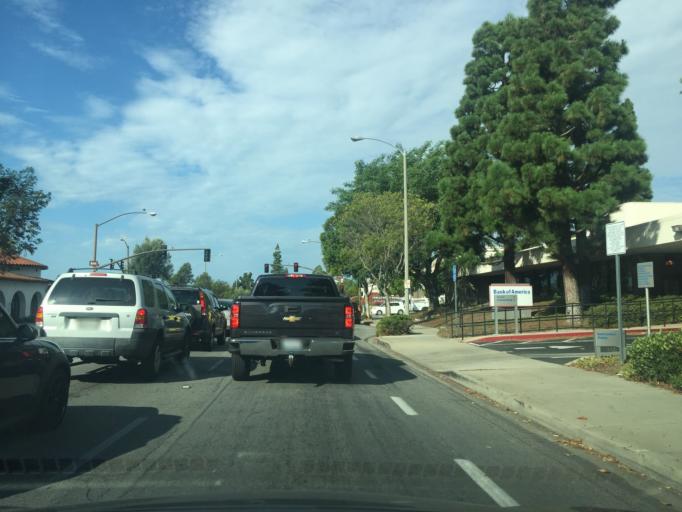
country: US
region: California
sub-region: Santa Barbara County
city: Mission Canyon
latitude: 34.4405
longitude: -119.7459
